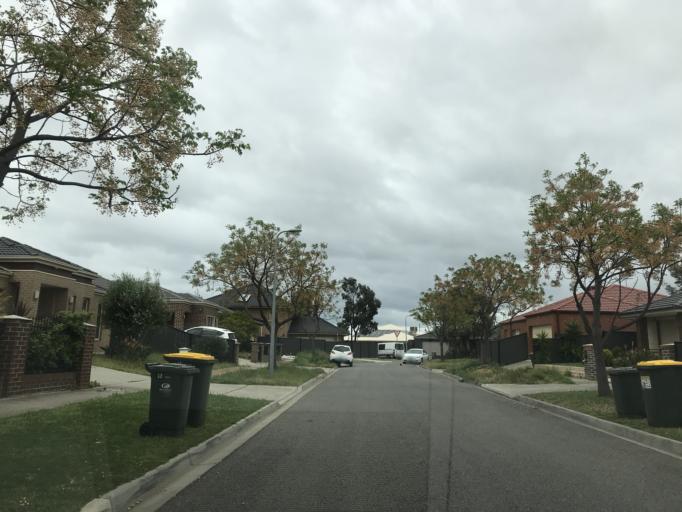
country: AU
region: Victoria
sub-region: Brimbank
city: Derrimut
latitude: -37.7866
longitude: 144.7598
